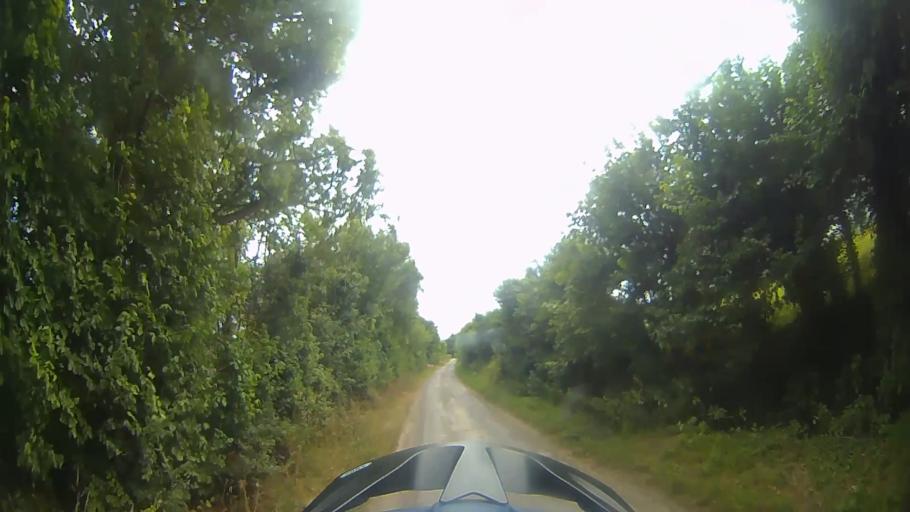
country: GB
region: England
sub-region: Oxfordshire
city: Wantage
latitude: 51.5680
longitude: -1.4475
